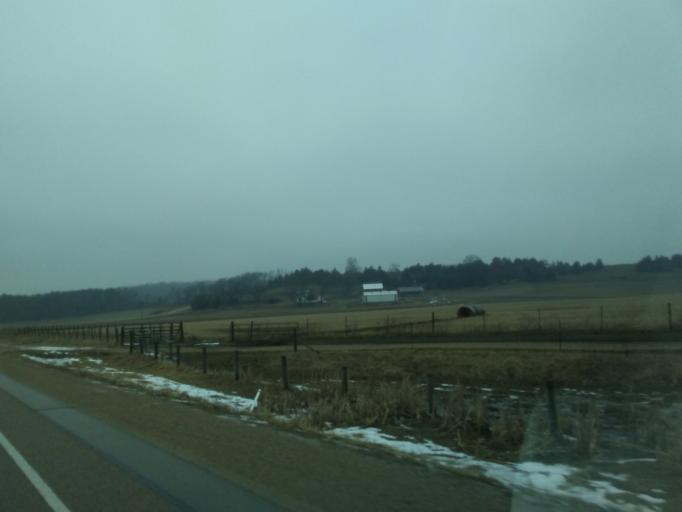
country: US
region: Wisconsin
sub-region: Dane County
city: Black Earth
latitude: 43.1255
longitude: -89.7061
